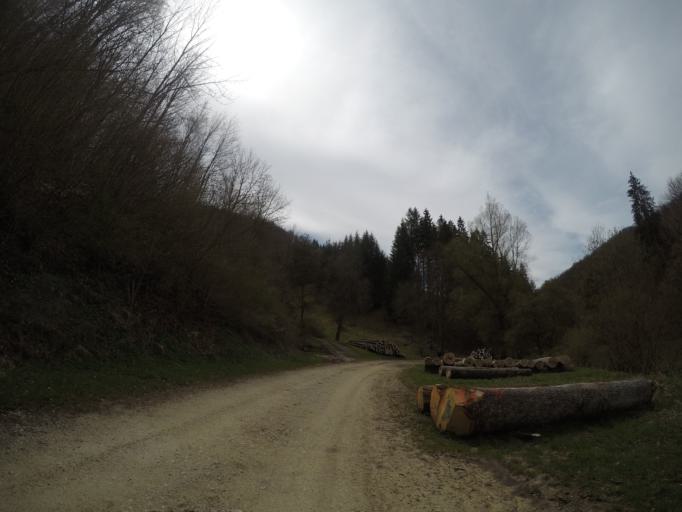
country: DE
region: Baden-Wuerttemberg
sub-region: Regierungsbezirk Stuttgart
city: Wiesensteig
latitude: 48.5524
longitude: 9.6035
